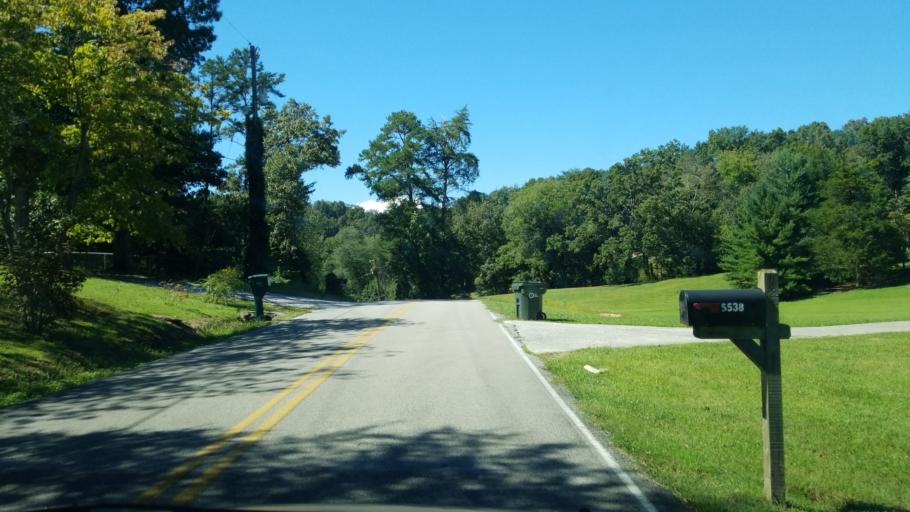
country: US
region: Tennessee
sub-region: Hamilton County
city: Collegedale
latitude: 35.0967
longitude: -85.0832
